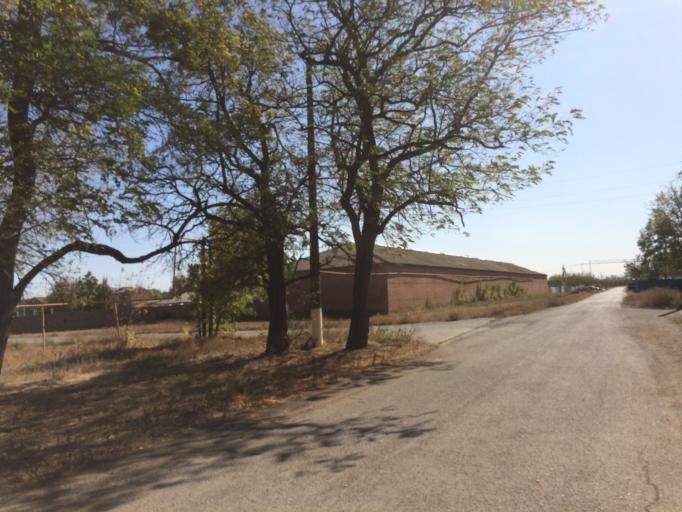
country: RU
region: Rostov
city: Gigant
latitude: 46.5157
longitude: 41.1887
